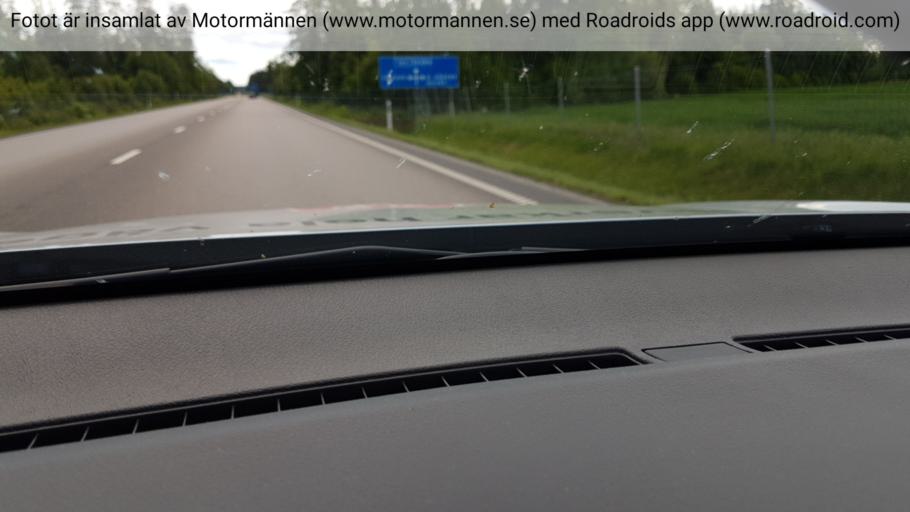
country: SE
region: Vaestra Goetaland
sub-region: Lidkopings Kommun
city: Vinninga
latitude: 58.4661
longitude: 13.2185
